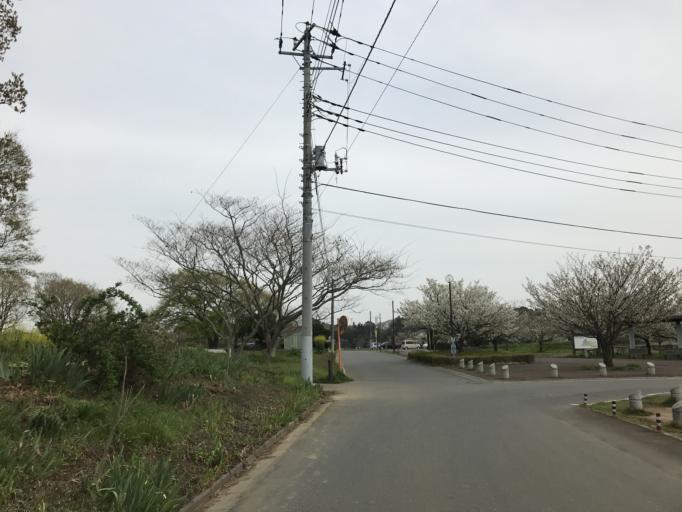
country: JP
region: Ibaraki
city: Moriya
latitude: 35.9514
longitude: 140.0050
